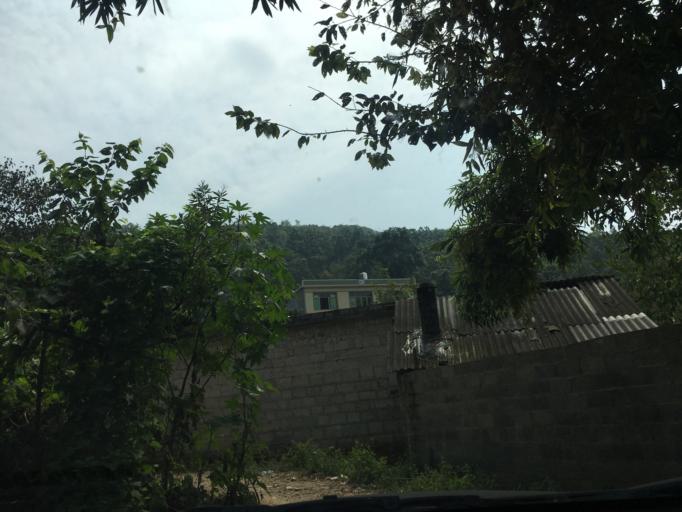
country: CN
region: Guizhou Sheng
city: Anshun
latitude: 25.5969
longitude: 105.6748
